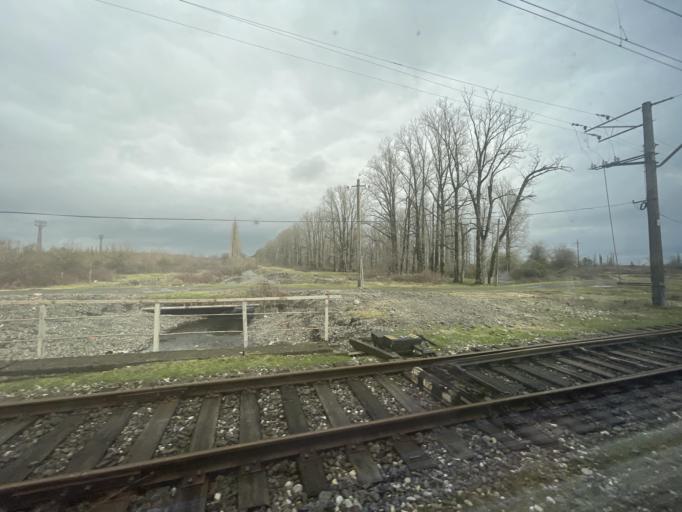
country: GE
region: Guria
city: Lanchkhuti
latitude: 42.0906
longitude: 42.0491
